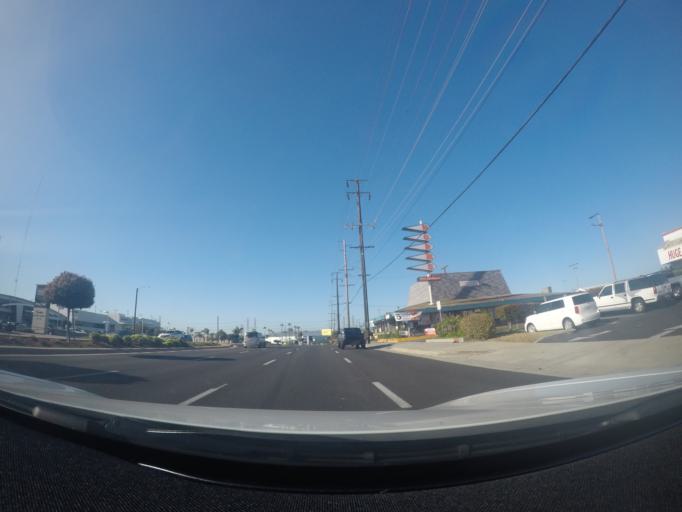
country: US
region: California
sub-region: Los Angeles County
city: Lawndale
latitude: 33.8615
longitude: -118.3527
